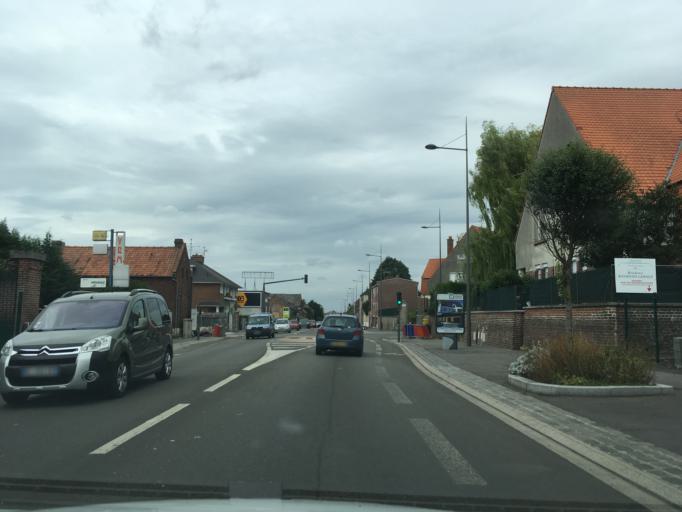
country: FR
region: Nord-Pas-de-Calais
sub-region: Departement du Nord
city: Cambrai
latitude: 50.1605
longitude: 3.2256
